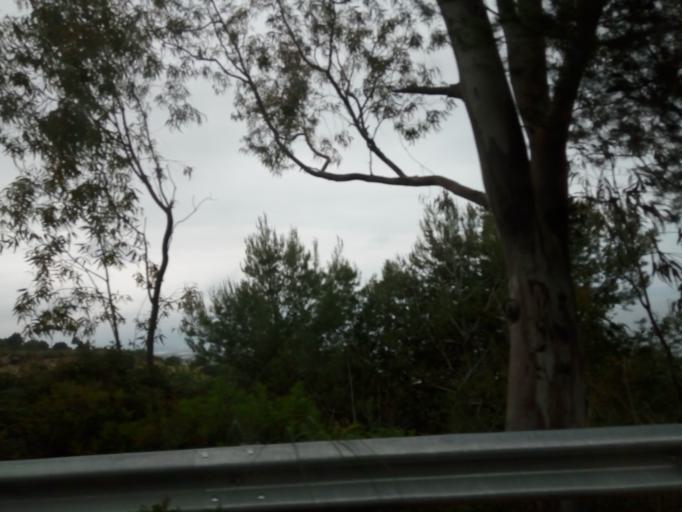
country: DZ
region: Tipaza
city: Tipasa
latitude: 36.5864
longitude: 2.5474
